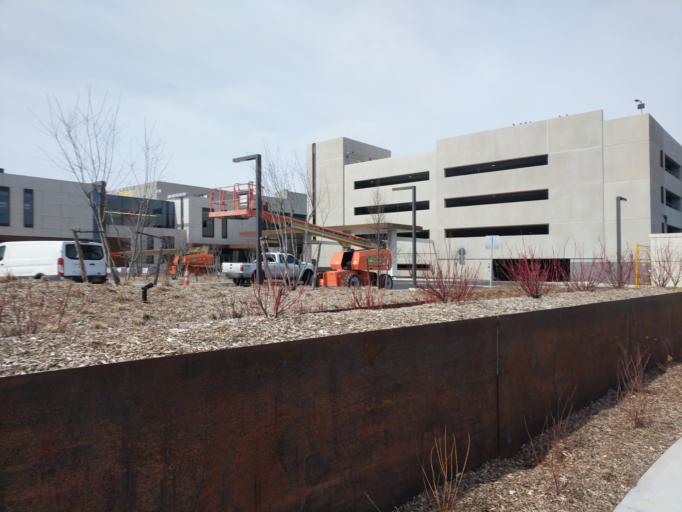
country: US
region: New York
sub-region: Nassau County
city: East Garden City
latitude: 40.7195
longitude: -73.5910
